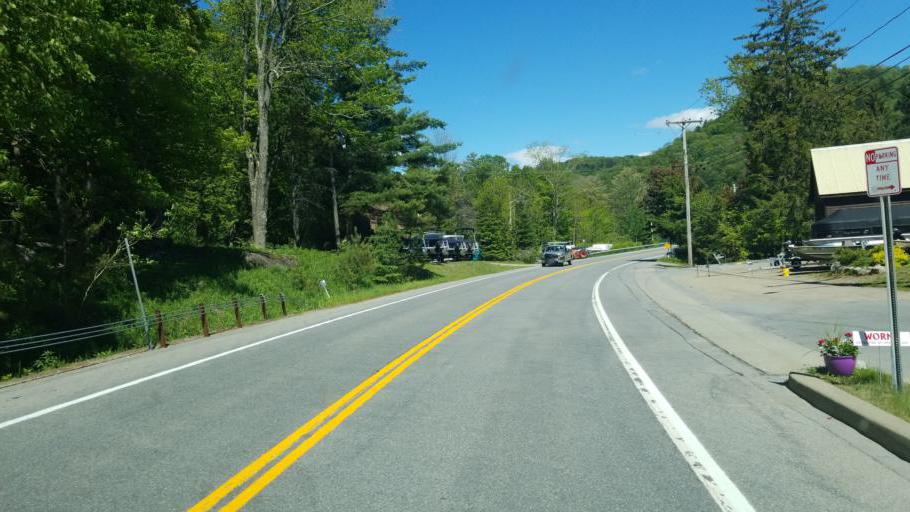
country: US
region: New York
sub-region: Fulton County
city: Gloversville
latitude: 43.1743
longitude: -74.5134
